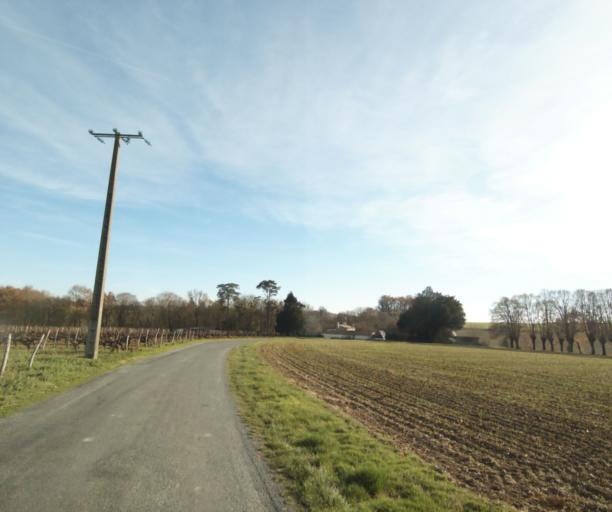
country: FR
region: Poitou-Charentes
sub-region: Departement de la Charente-Maritime
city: Chaniers
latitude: 45.7325
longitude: -0.5491
